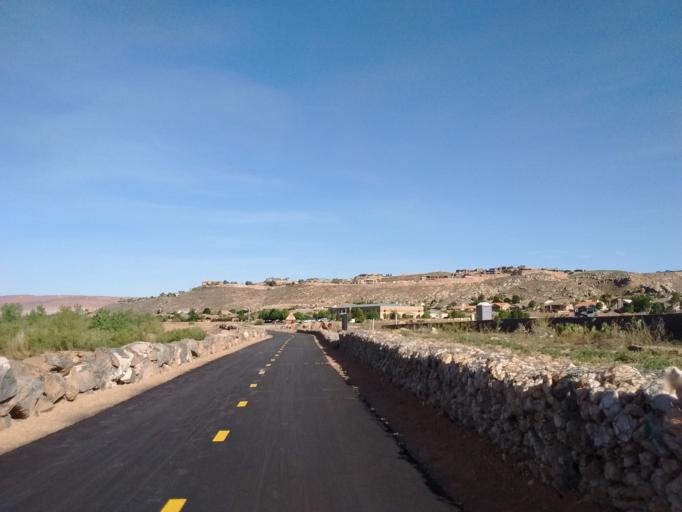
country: US
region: Utah
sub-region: Washington County
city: Saint George
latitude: 37.0855
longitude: -113.5548
